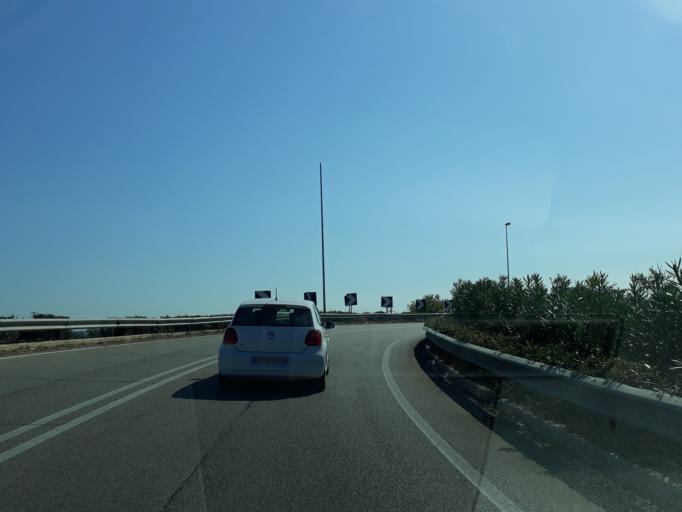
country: IT
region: Apulia
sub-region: Provincia di Bari
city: Monopoli
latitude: 40.9240
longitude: 17.3169
